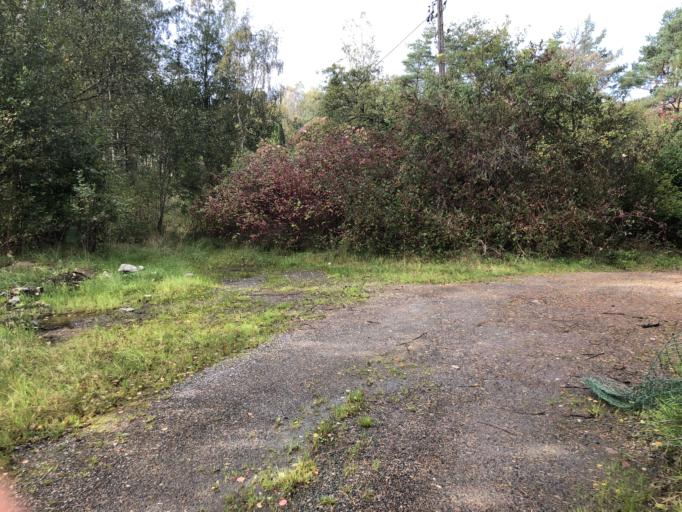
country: SE
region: Vaestra Goetaland
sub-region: Goteborg
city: Majorna
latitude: 57.7361
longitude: 11.8570
